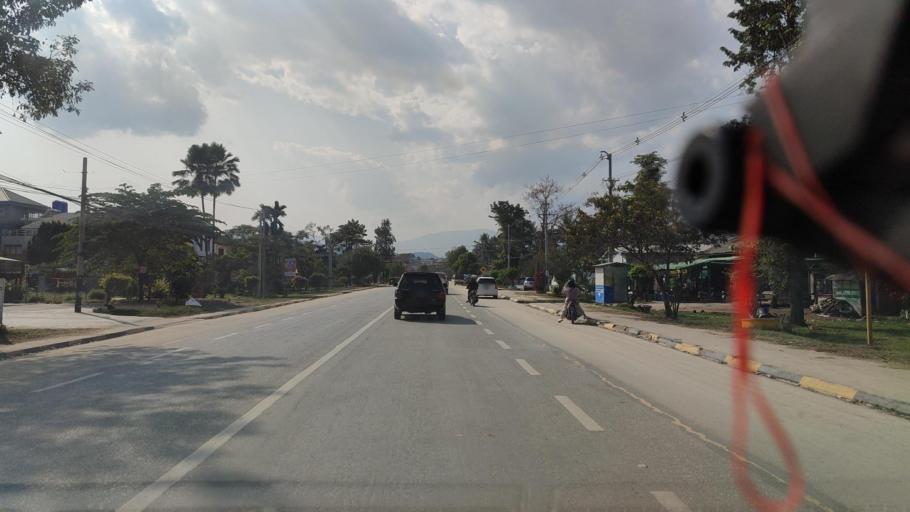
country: TH
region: Chiang Rai
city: Mae Sai
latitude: 21.2989
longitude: 99.6179
